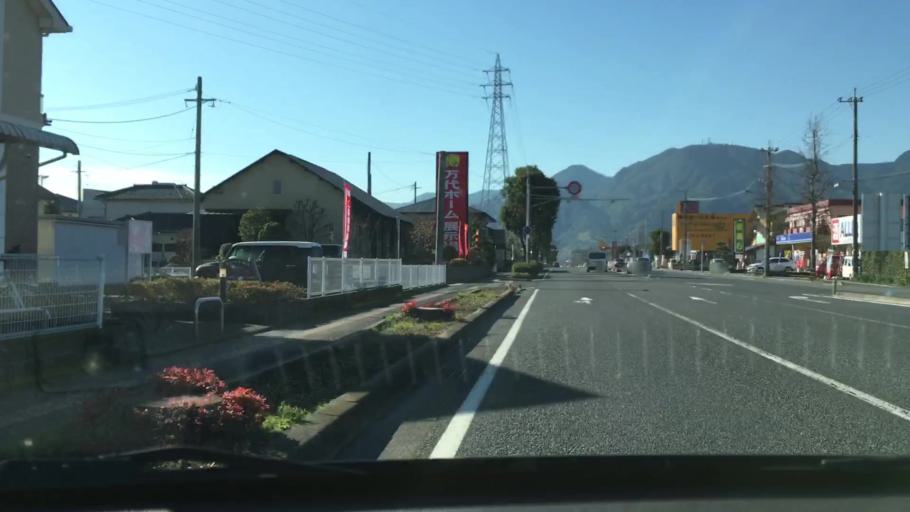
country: JP
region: Kagoshima
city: Kajiki
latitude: 31.7247
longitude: 130.6235
